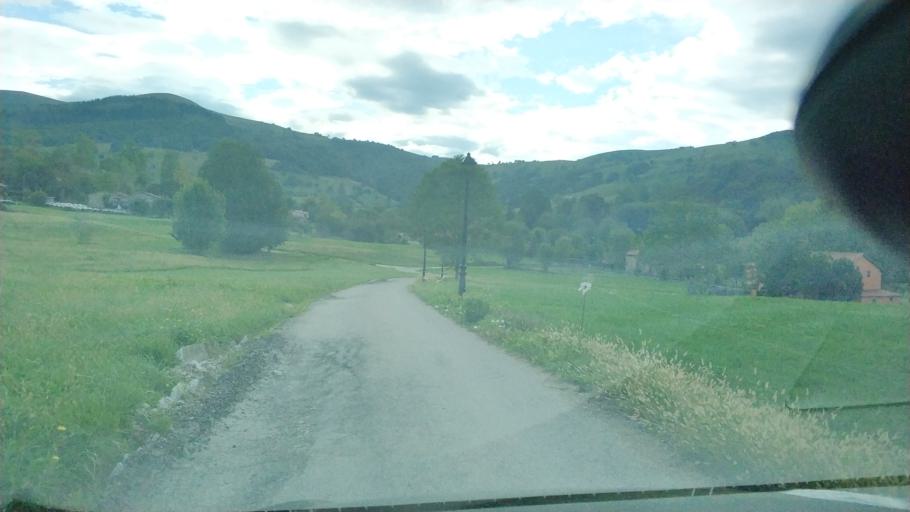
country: ES
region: Cantabria
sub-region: Provincia de Cantabria
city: Santa Maria de Cayon
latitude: 43.2841
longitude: -3.8114
